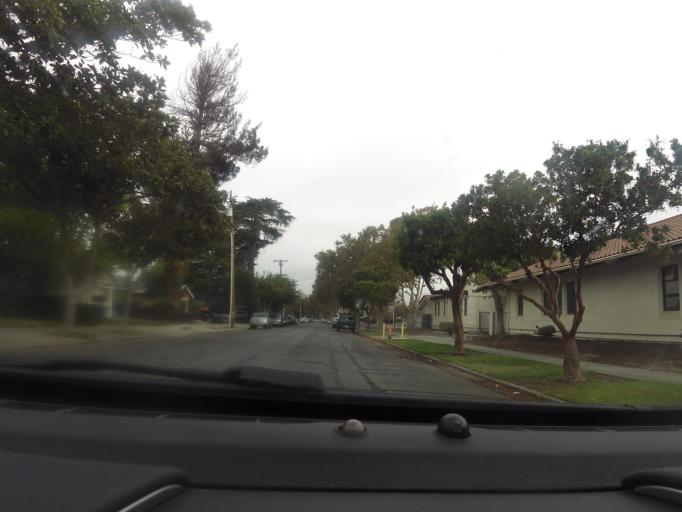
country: US
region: California
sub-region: San Benito County
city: Hollister
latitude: 36.8413
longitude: -121.4060
